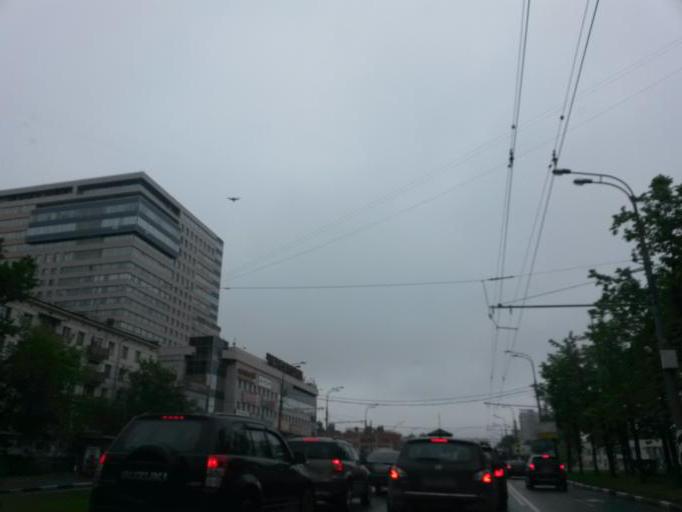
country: RU
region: Moskovskaya
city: Cheremushki
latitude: 55.6685
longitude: 37.5529
